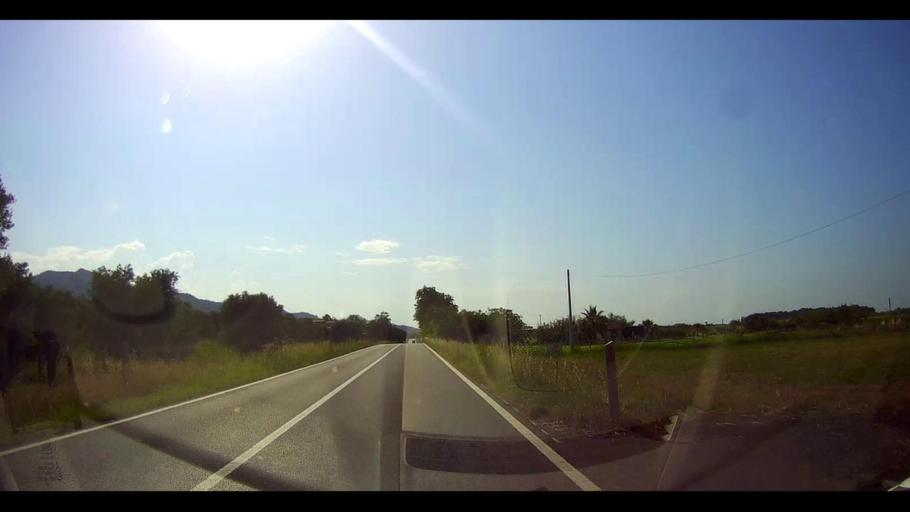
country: IT
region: Calabria
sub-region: Provincia di Cosenza
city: Cariati
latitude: 39.4794
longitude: 16.9935
